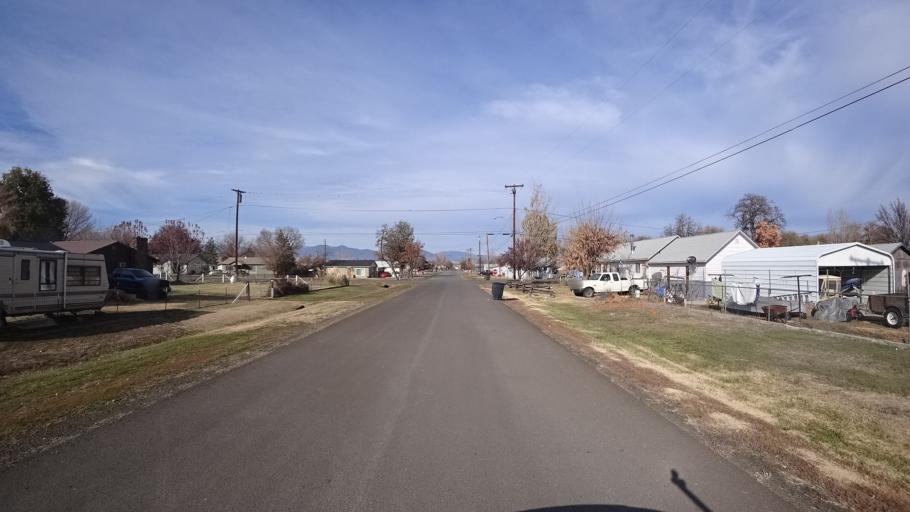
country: US
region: California
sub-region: Siskiyou County
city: Montague
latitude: 41.7244
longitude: -122.5257
